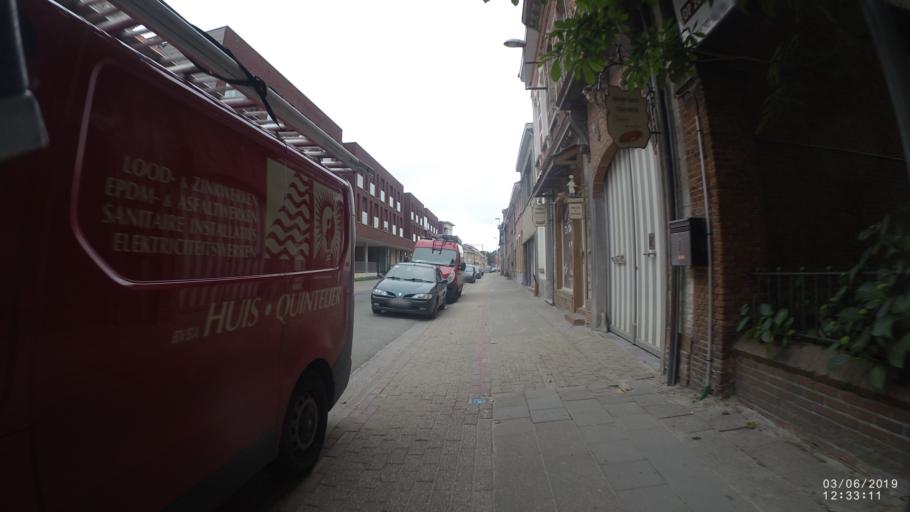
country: BE
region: Flanders
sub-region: Provincie Oost-Vlaanderen
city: Sint-Niklaas
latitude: 51.1558
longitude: 4.1474
